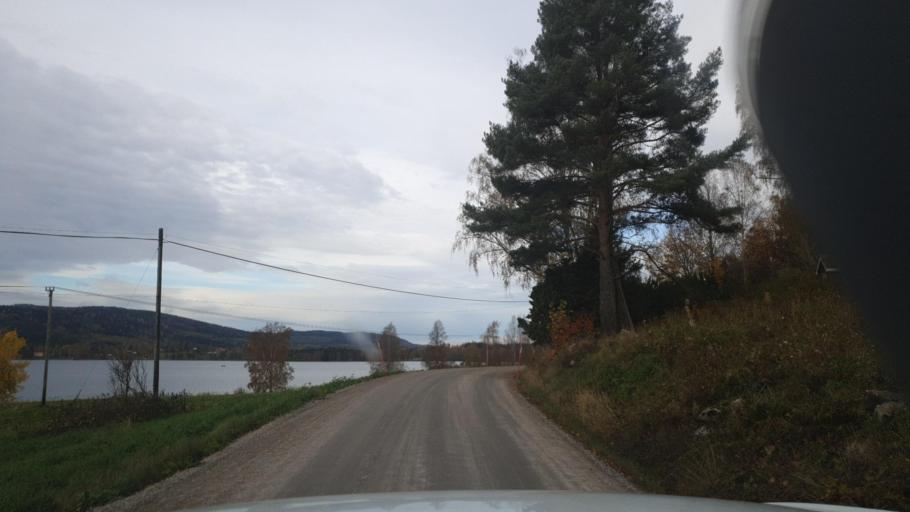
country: SE
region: Vaermland
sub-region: Arvika Kommun
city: Arvika
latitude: 59.7299
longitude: 12.8336
